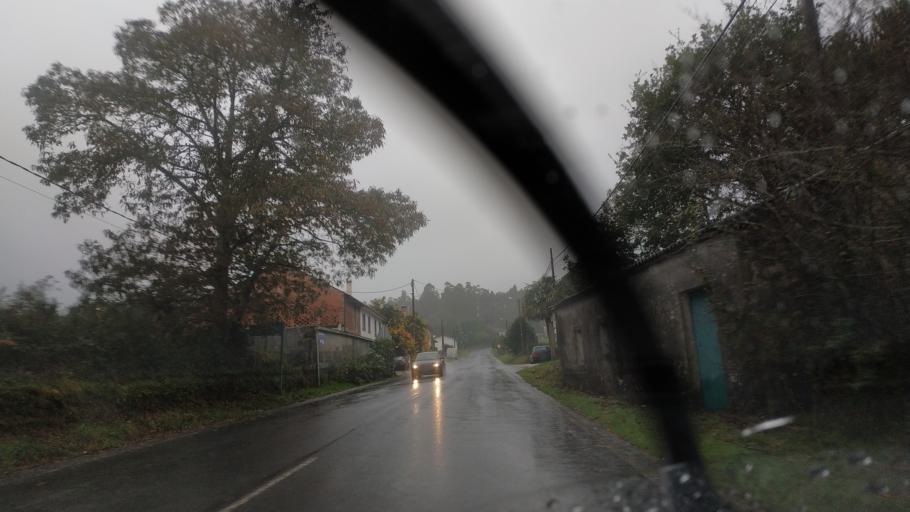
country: ES
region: Galicia
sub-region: Provincia da Coruna
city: Negreira
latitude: 42.9105
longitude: -8.7593
